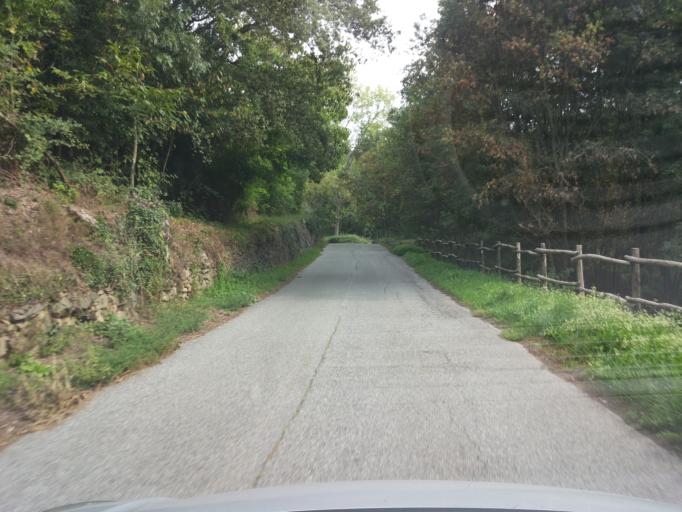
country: IT
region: Piedmont
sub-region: Provincia di Biella
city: Roppolo
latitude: 45.4211
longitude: 8.0804
